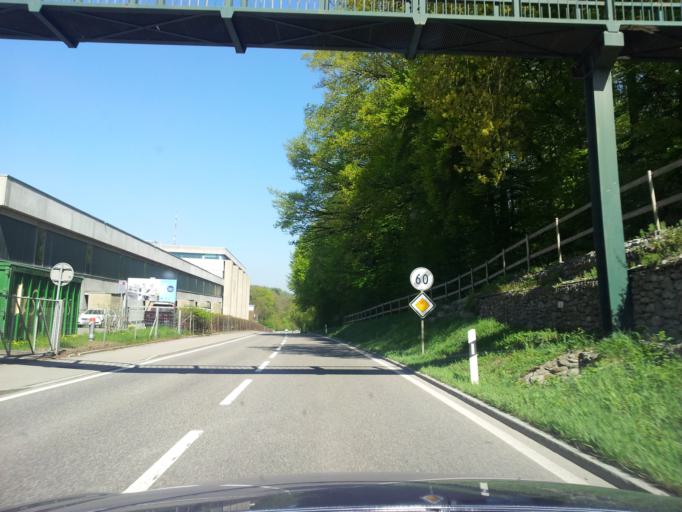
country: CH
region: Zurich
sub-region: Bezirk Dietikon
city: Urdorf / Oberurdorf
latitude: 47.3668
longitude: 8.4293
